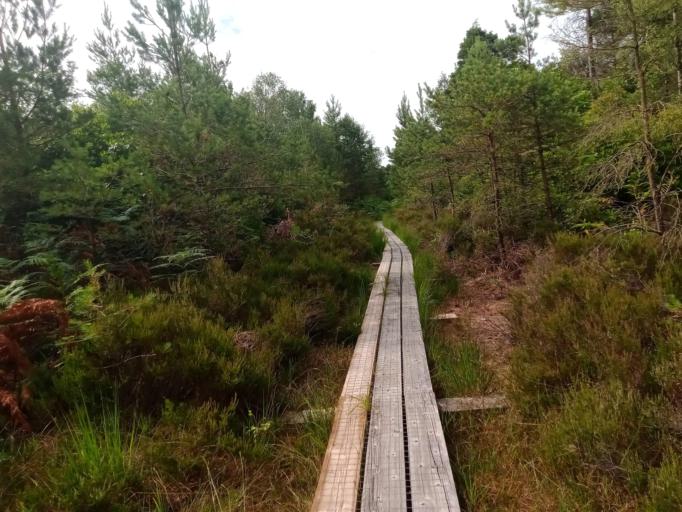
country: IE
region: Leinster
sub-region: Laois
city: Abbeyleix
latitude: 52.8932
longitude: -7.3605
